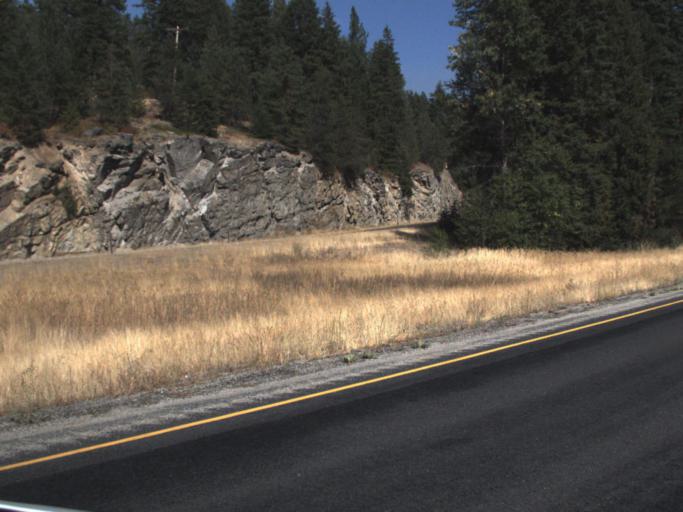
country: US
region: Washington
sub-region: Spokane County
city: Deer Park
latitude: 48.0960
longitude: -117.3112
